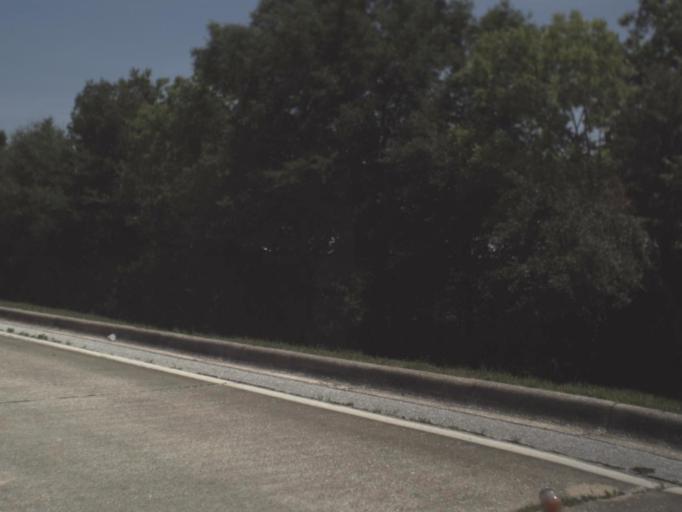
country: US
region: Florida
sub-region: Duval County
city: Jacksonville
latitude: 30.2969
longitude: -81.6141
